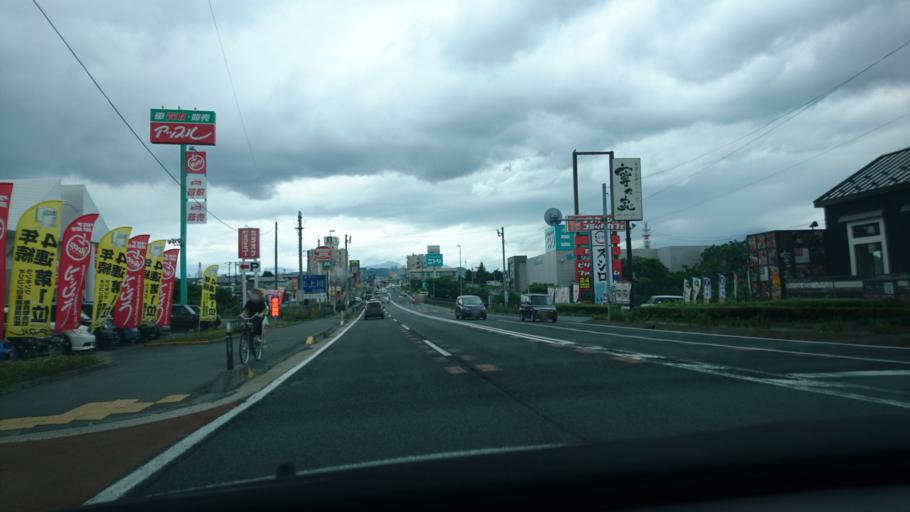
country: JP
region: Iwate
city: Morioka-shi
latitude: 39.7240
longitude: 141.1300
